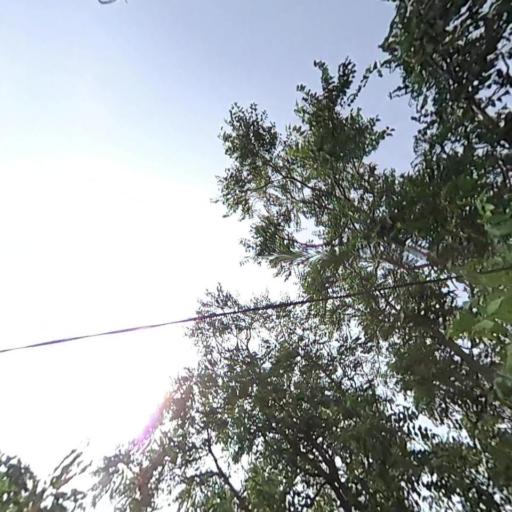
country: IN
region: Telangana
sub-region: Nalgonda
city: Nalgonda
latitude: 17.2108
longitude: 79.1576
